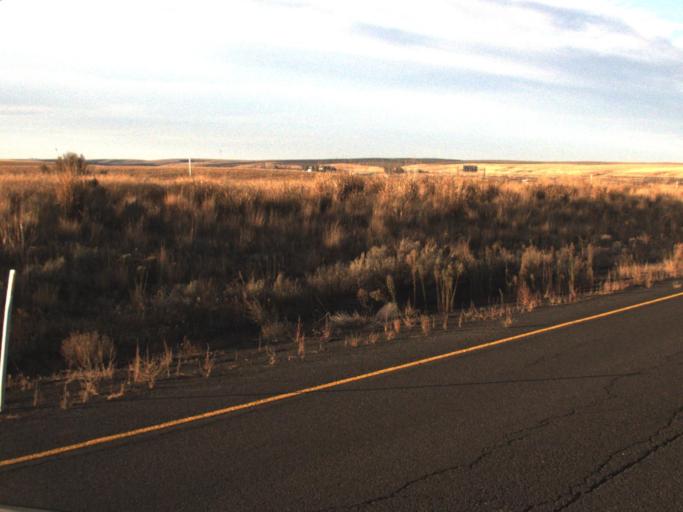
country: US
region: Washington
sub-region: Adams County
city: Ritzville
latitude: 47.1065
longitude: -118.4034
